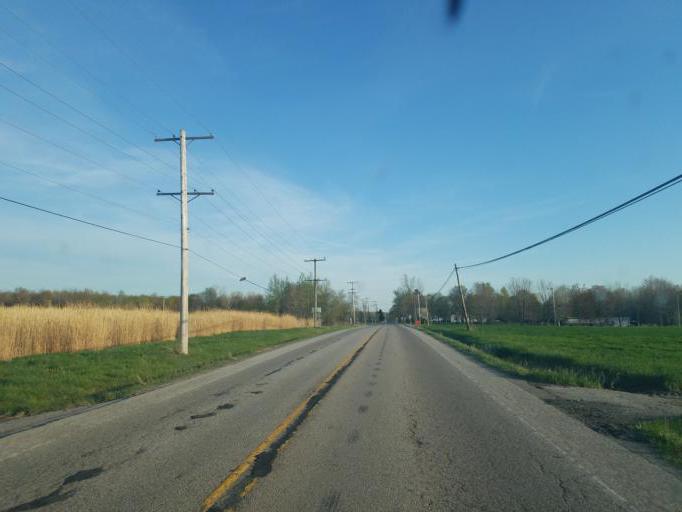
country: US
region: Ohio
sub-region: Ashtabula County
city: Andover
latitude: 41.7653
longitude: -80.5715
